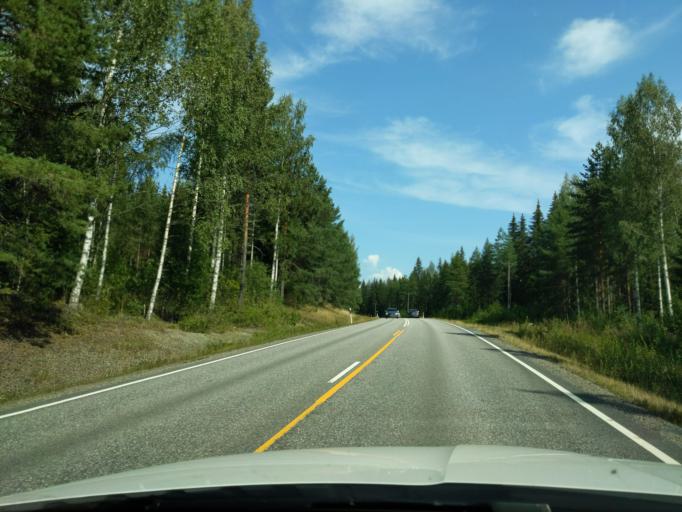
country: FI
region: Paijanne Tavastia
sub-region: Lahti
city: Padasjoki
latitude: 61.3306
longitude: 25.2101
